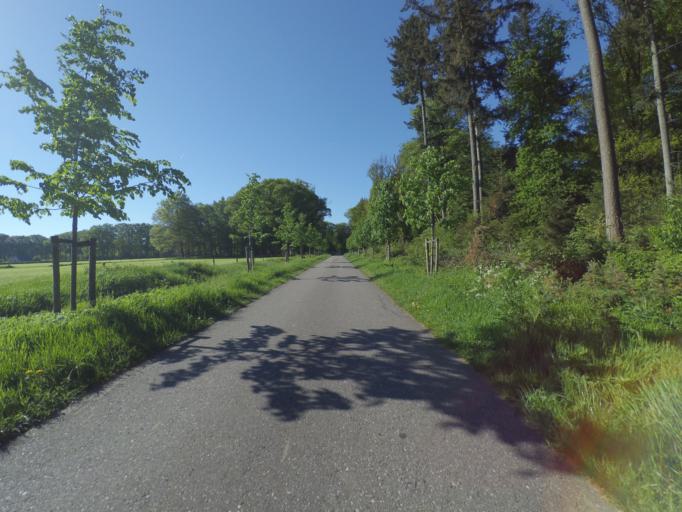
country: NL
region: Gelderland
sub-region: Gemeente Voorst
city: Voorst
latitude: 52.1896
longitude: 6.1163
